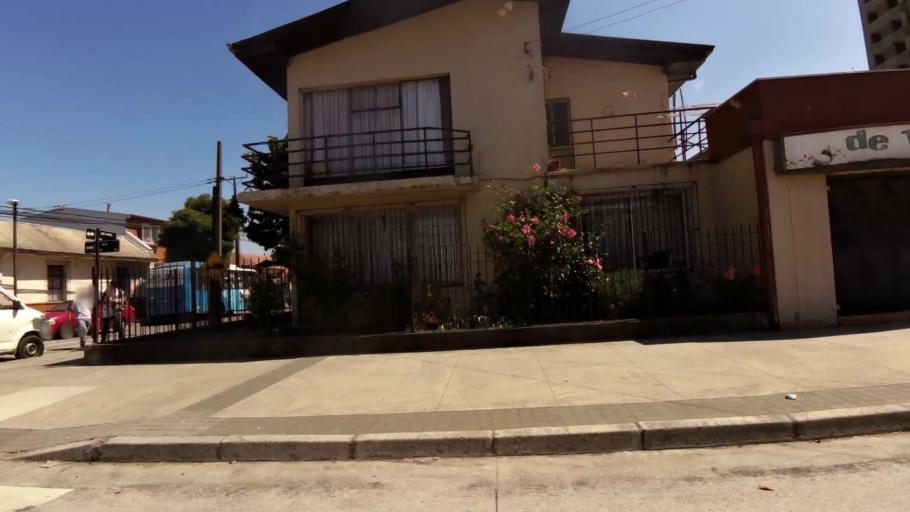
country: CL
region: Biobio
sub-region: Provincia de Concepcion
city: Concepcion
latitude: -36.8207
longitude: -73.0615
